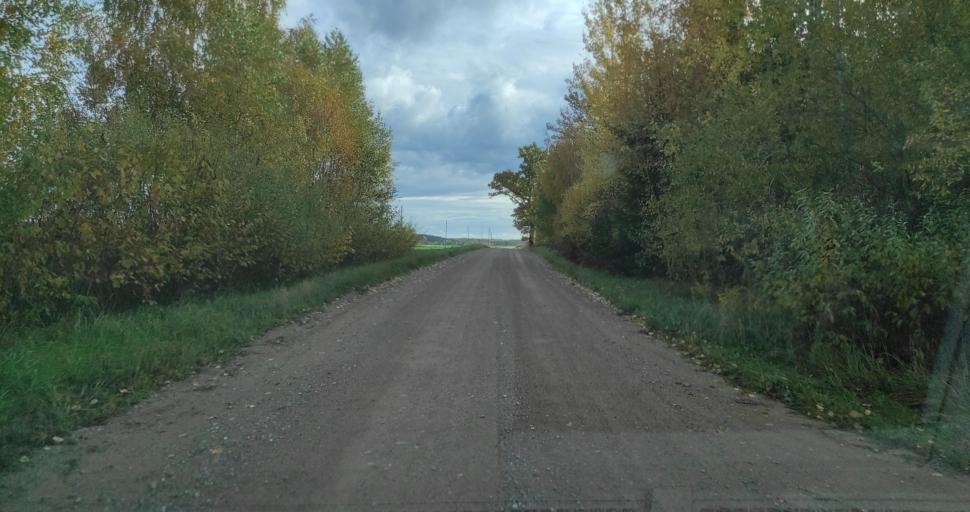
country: LV
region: Skrunda
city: Skrunda
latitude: 56.6124
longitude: 21.9556
